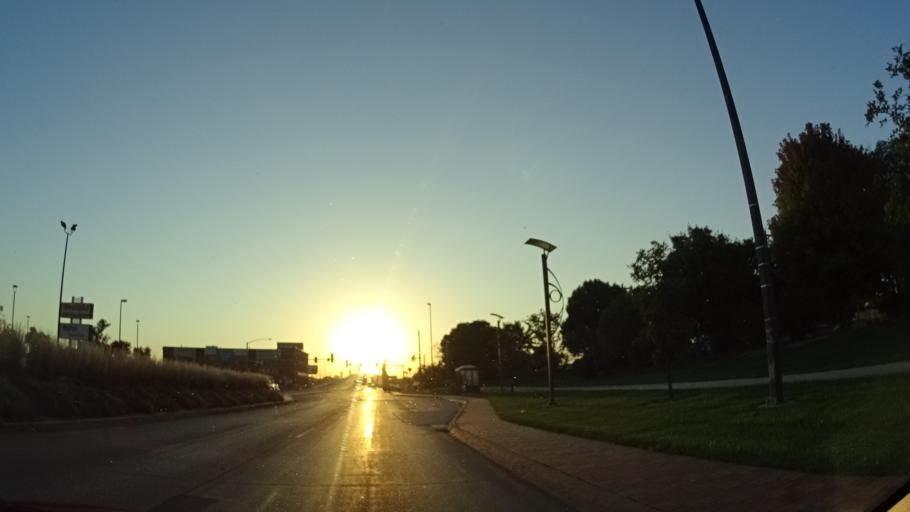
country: US
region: Iowa
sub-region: Pottawattamie County
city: Council Bluffs
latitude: 41.2620
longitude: -95.8545
